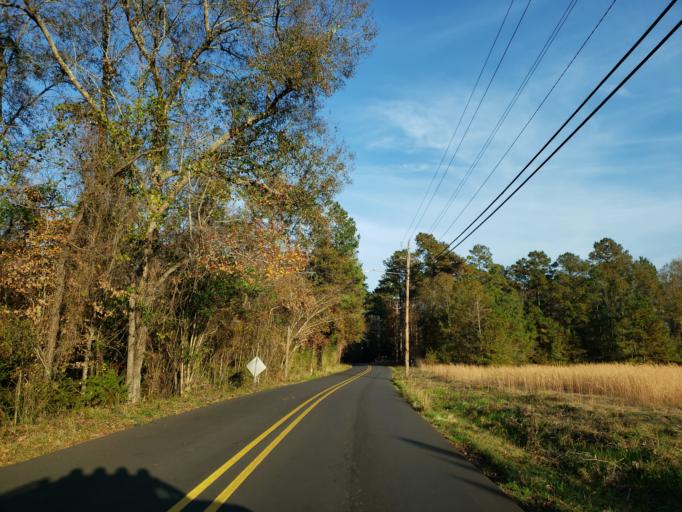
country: US
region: Mississippi
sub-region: Lamar County
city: Arnold Line
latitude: 31.3482
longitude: -89.3581
